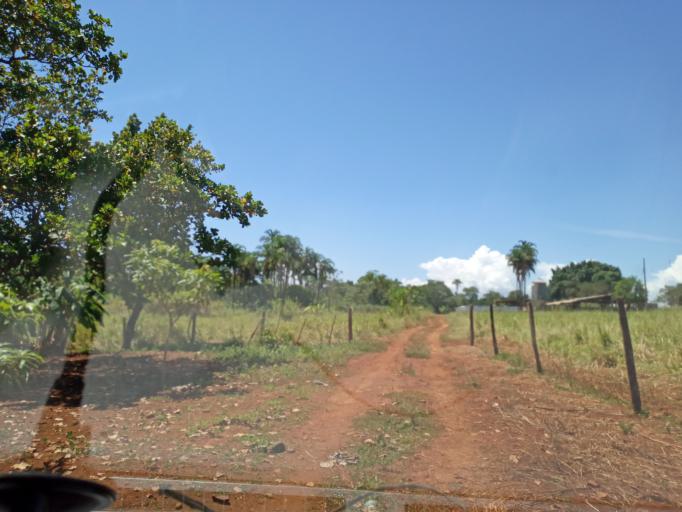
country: BR
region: Goias
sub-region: Itumbiara
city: Itumbiara
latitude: -18.4356
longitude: -49.1691
